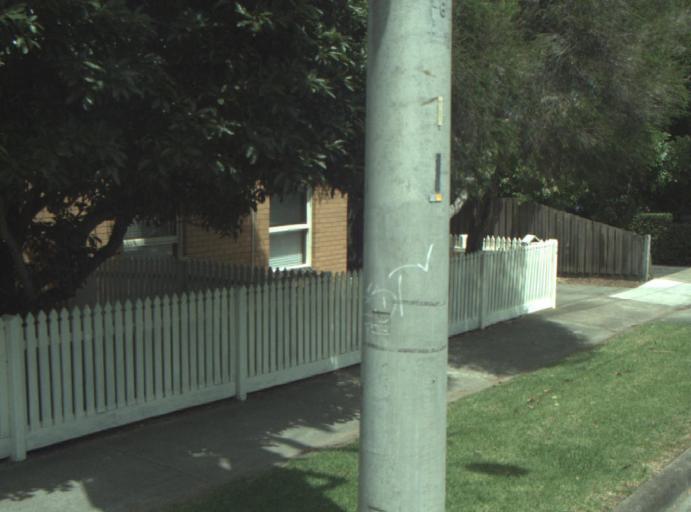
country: AU
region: Victoria
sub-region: Greater Geelong
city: Breakwater
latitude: -38.1791
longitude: 144.3410
